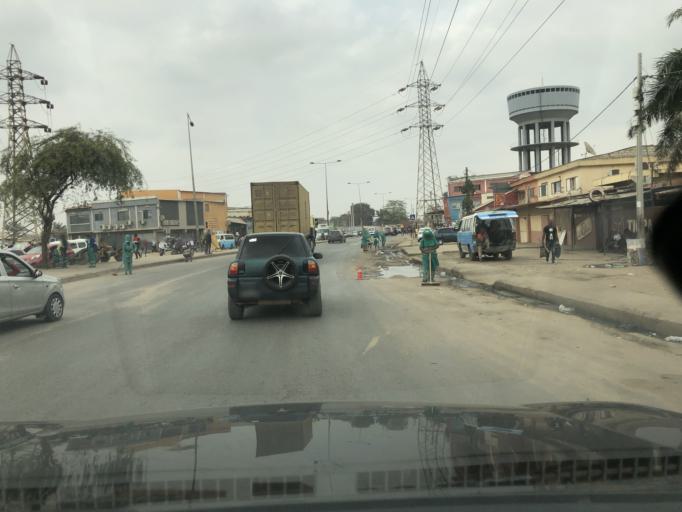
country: AO
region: Luanda
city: Luanda
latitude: -8.8202
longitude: 13.2810
